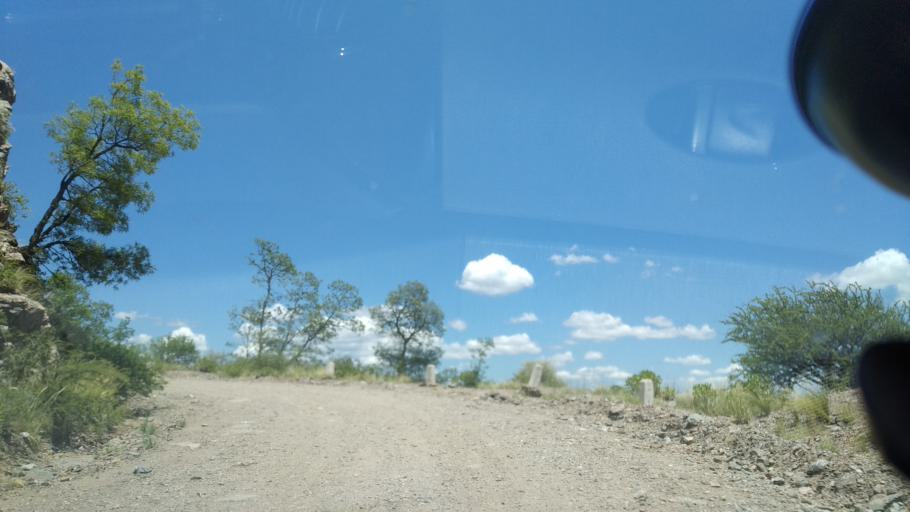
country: AR
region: Cordoba
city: Salsacate
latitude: -31.3745
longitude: -65.4074
